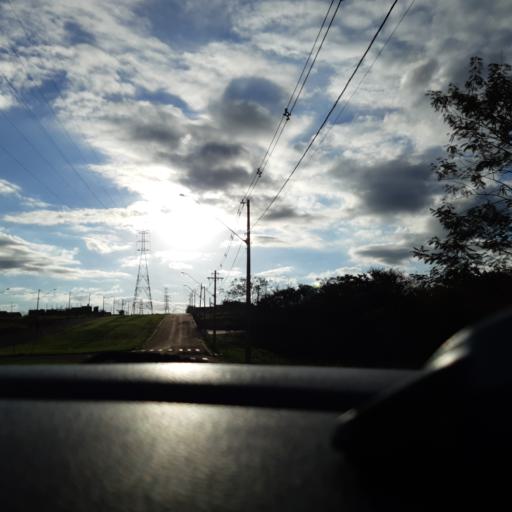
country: BR
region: Sao Paulo
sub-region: Ourinhos
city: Ourinhos
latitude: -22.9990
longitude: -49.8480
